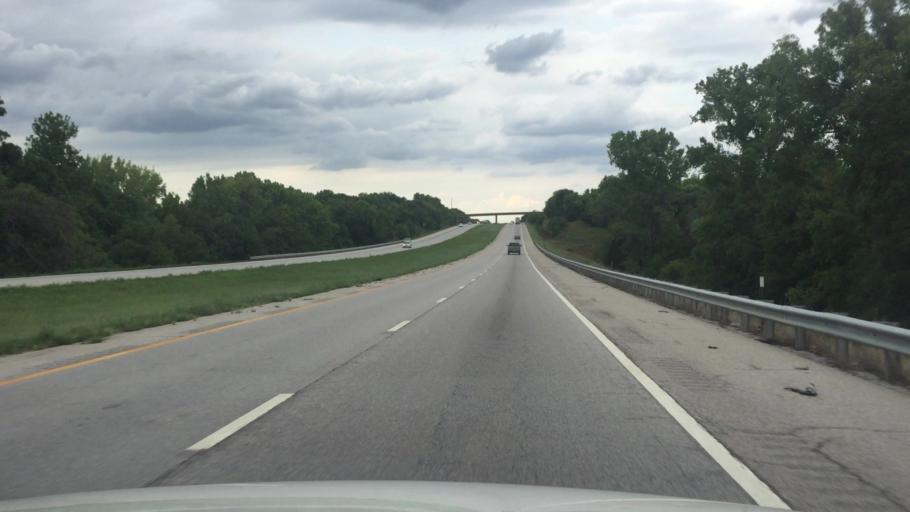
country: US
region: Missouri
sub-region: Cass County
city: Belton
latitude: 38.7907
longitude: -94.6766
